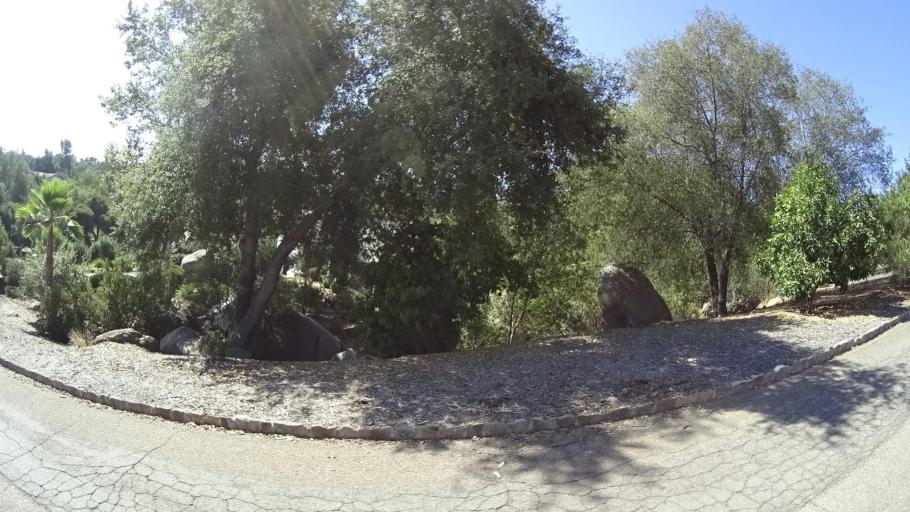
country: US
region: California
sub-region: San Diego County
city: Hidden Meadows
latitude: 33.2105
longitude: -117.1123
